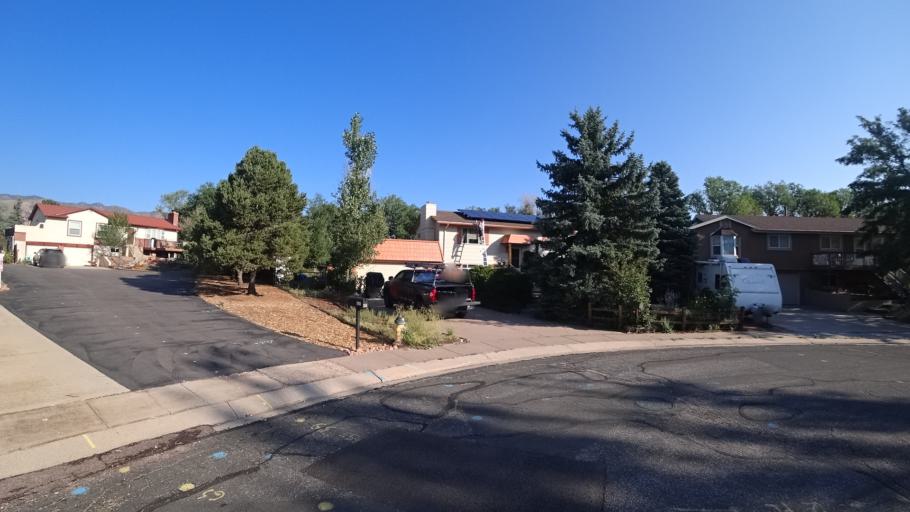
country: US
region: Colorado
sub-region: El Paso County
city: Colorado Springs
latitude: 38.8926
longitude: -104.8478
